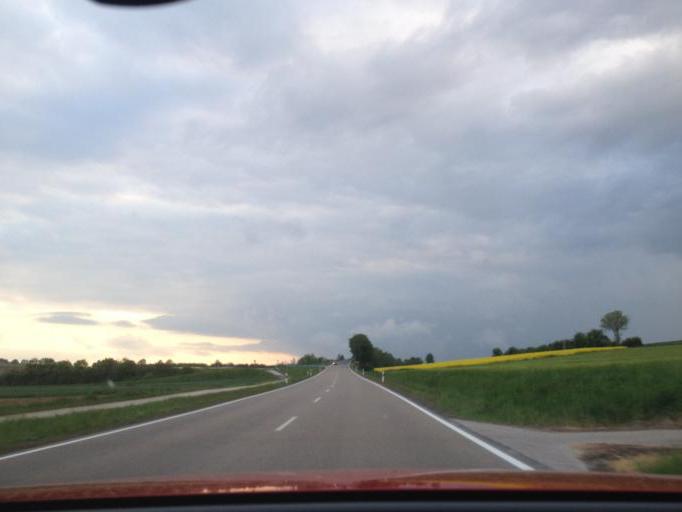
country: DE
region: Bavaria
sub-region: Upper Palatinate
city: Gebenbach
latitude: 49.5371
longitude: 11.9066
